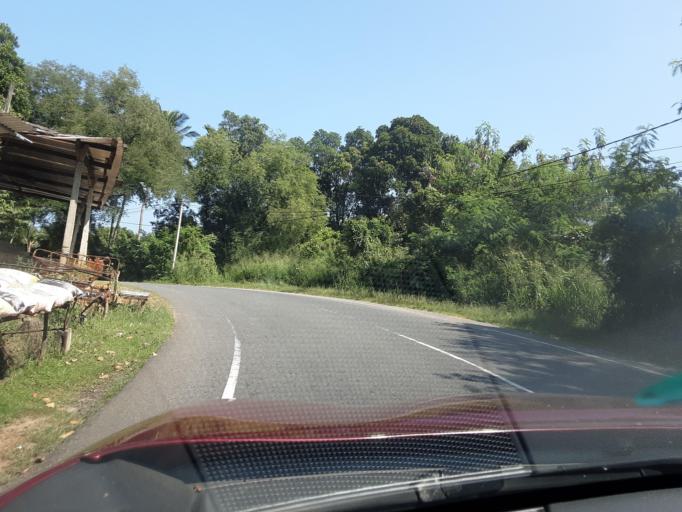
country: LK
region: Uva
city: Badulla
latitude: 7.1569
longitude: 81.0544
